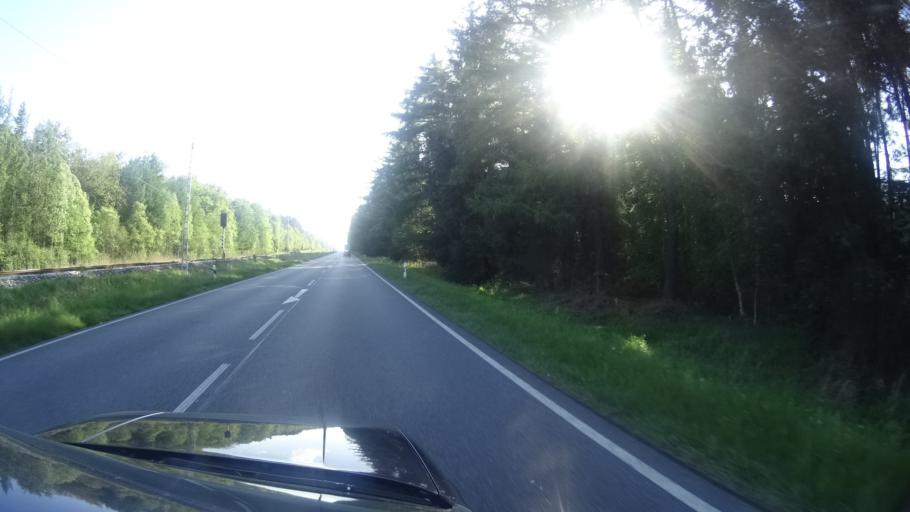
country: DE
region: Mecklenburg-Vorpommern
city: Gelbensande
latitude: 54.1926
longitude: 12.2885
